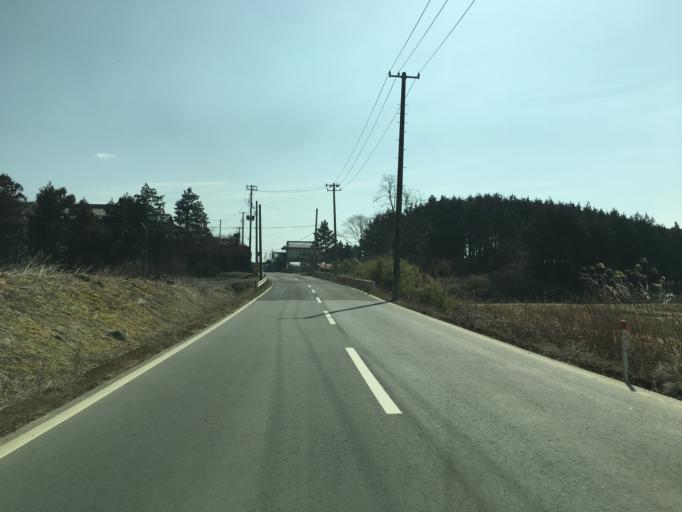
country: JP
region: Fukushima
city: Ishikawa
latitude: 37.1541
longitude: 140.3894
